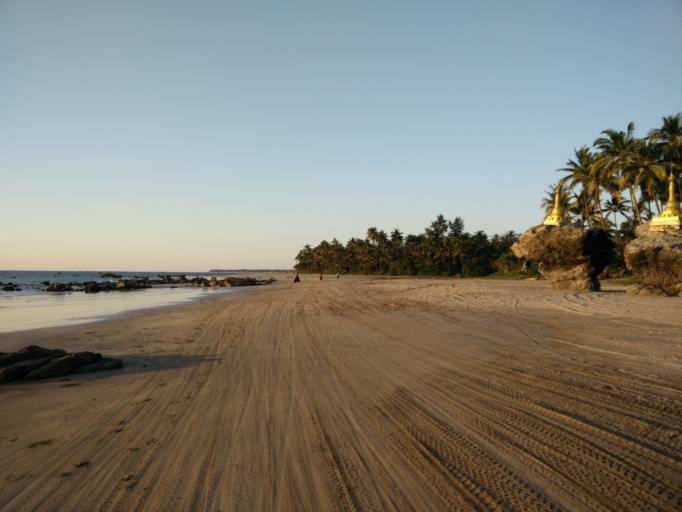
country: MM
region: Ayeyarwady
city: Pathein
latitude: 16.8338
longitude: 94.3929
